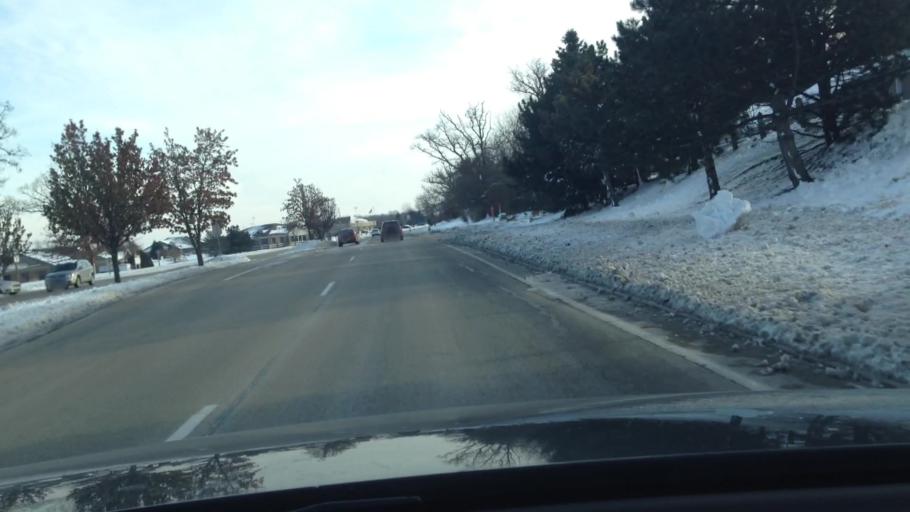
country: US
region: Wisconsin
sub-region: Walworth County
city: Lake Geneva
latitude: 42.5888
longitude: -88.4139
